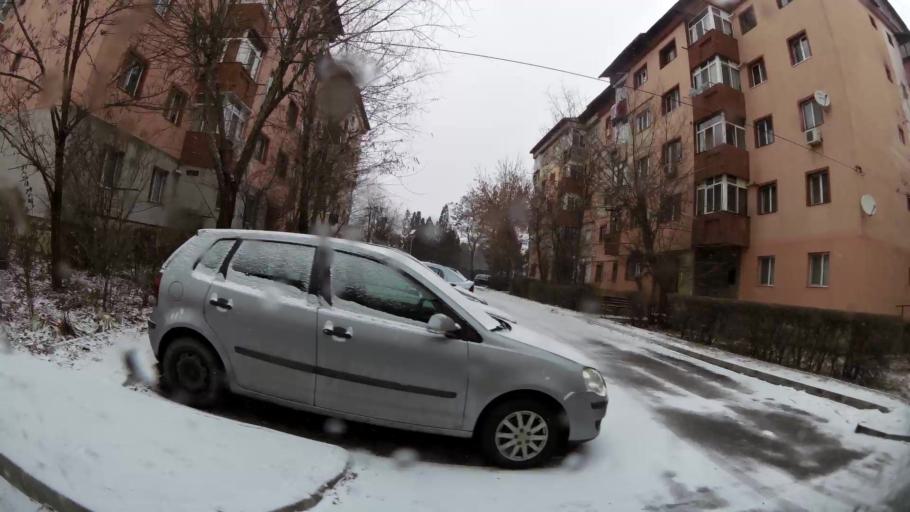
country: RO
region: Dambovita
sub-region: Municipiul Targoviste
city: Targoviste
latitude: 44.9141
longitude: 25.4726
